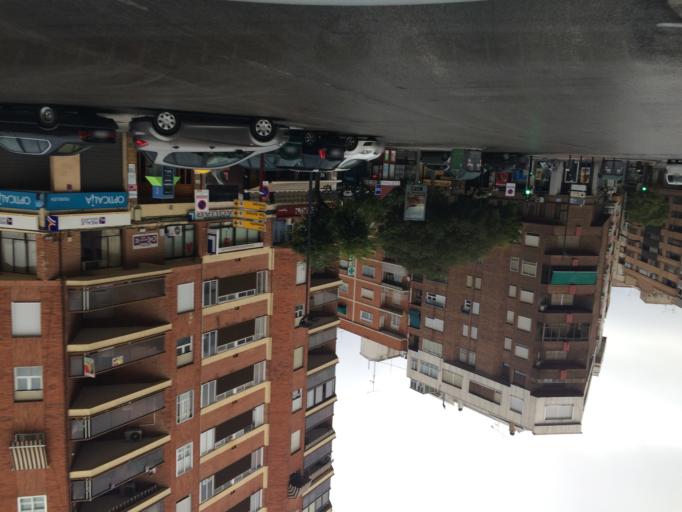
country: ES
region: Castille-La Mancha
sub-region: Provincia de Albacete
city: Albacete
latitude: 38.9996
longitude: -1.8614
